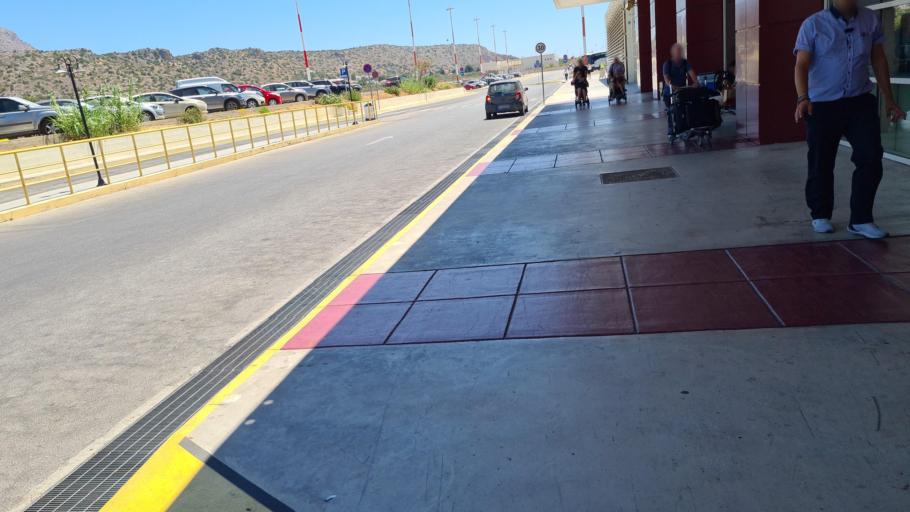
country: GR
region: Crete
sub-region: Nomos Chanias
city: Mouzouras
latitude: 35.5400
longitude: 24.1413
